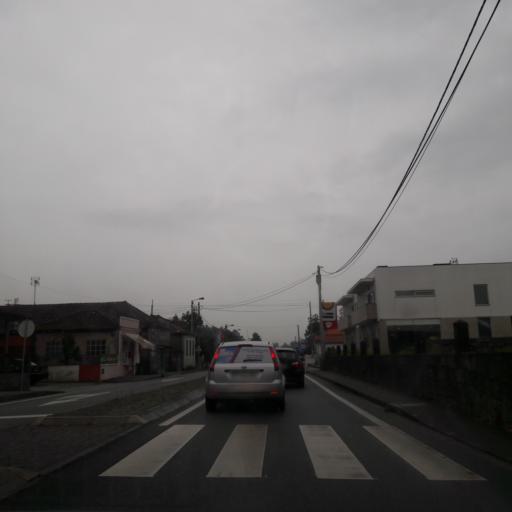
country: PT
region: Porto
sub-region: Vila do Conde
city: Arvore
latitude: 41.3165
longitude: -8.7100
